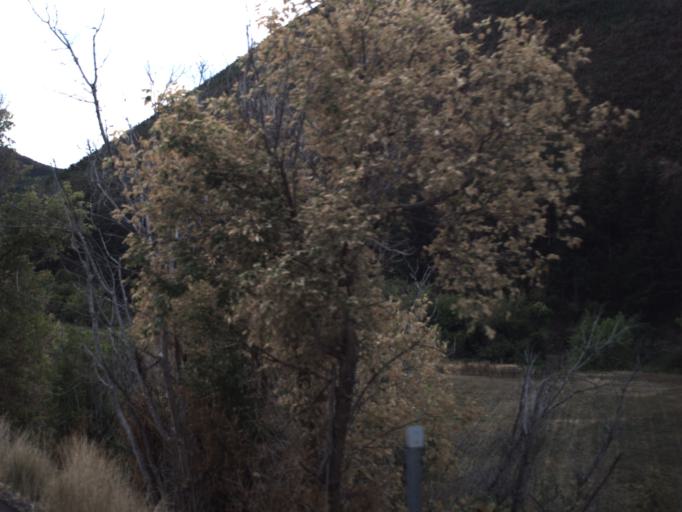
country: US
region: Utah
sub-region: Morgan County
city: Morgan
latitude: 40.9327
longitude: -111.6230
